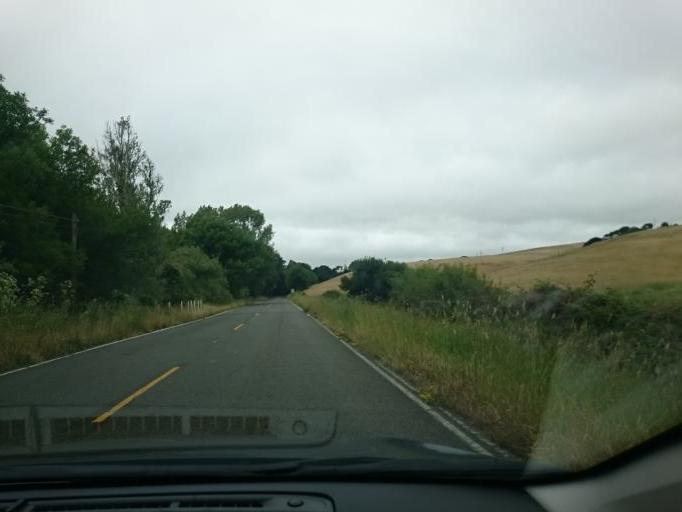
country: US
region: California
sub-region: Marin County
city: Lagunitas-Forest Knolls
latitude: 38.0338
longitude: -122.7823
